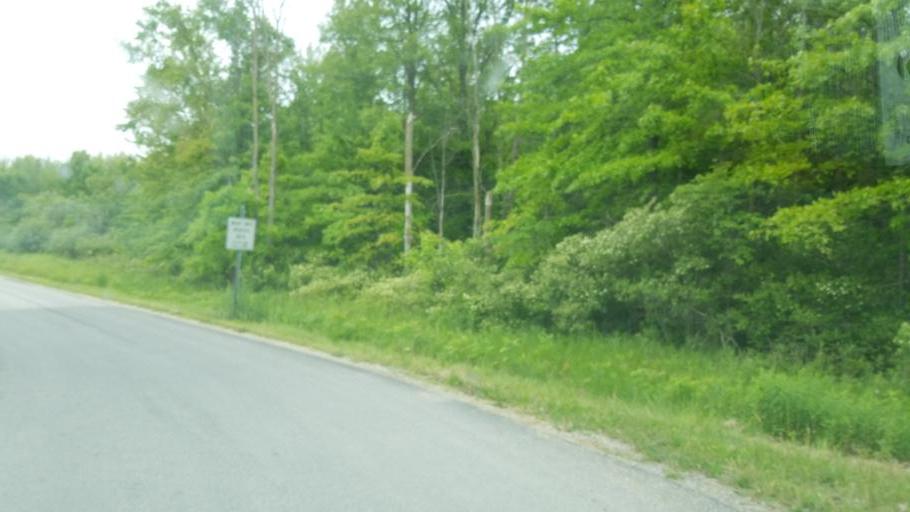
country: US
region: Ohio
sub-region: Knox County
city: Centerburg
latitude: 40.3077
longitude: -82.7483
